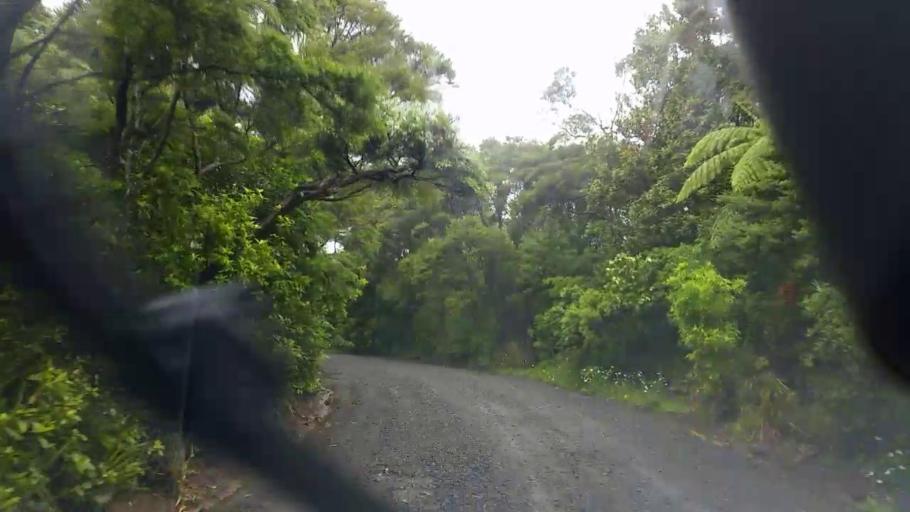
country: NZ
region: Auckland
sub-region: Auckland
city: Waitakere
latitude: -36.9112
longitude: 174.5450
